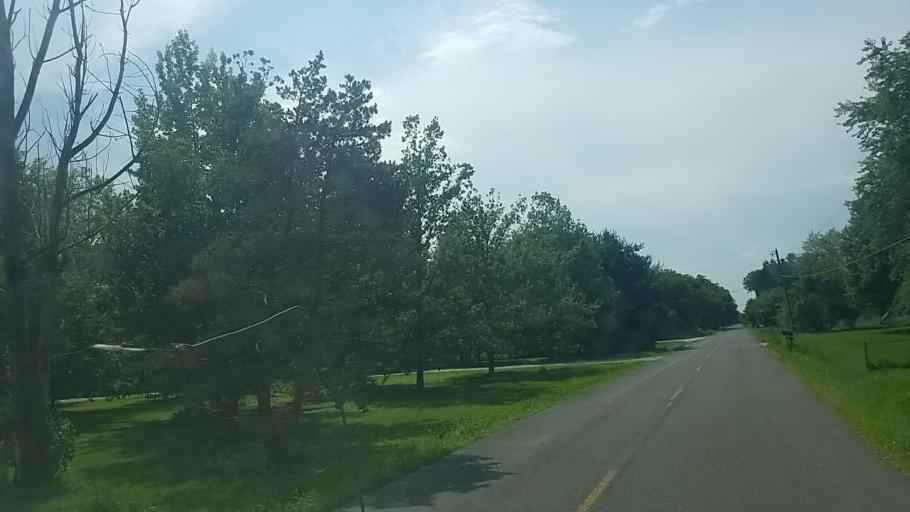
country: US
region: Ohio
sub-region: Medina County
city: Westfield Center
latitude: 41.0899
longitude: -81.9651
